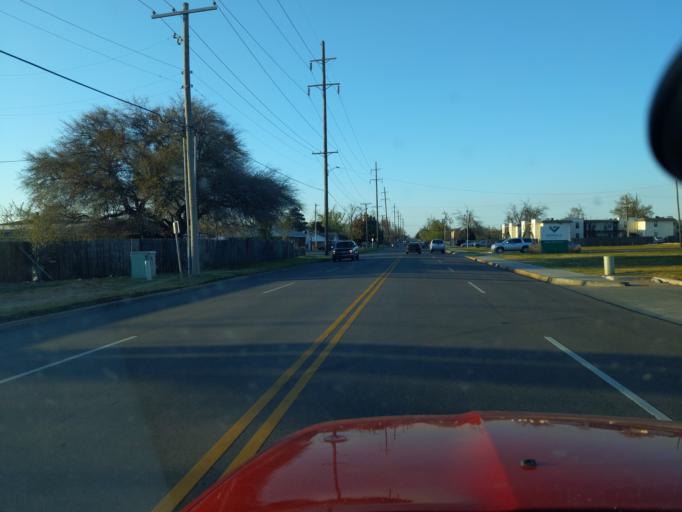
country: US
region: Oklahoma
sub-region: Oklahoma County
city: Oklahoma City
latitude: 35.4079
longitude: -97.5213
